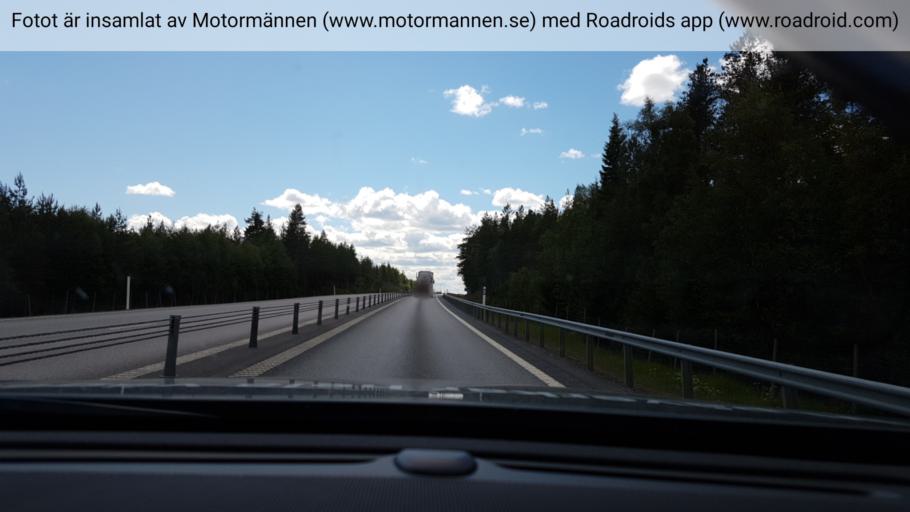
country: SE
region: Vaesterbotten
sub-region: Umea Kommun
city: Saevar
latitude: 63.9036
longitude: 20.5770
